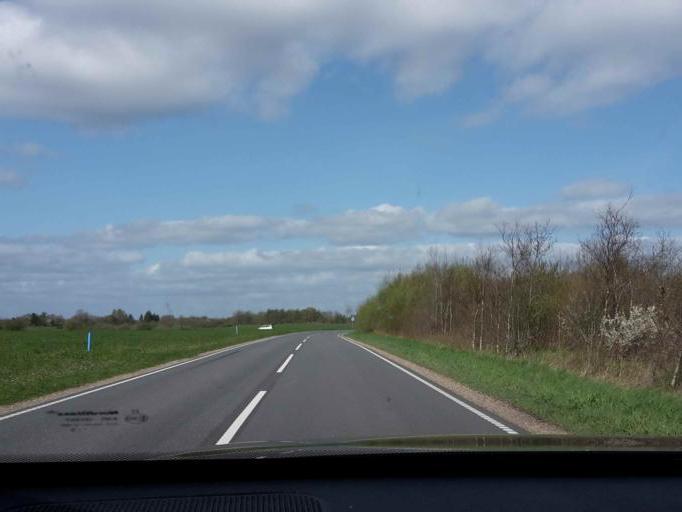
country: DK
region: South Denmark
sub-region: Billund Kommune
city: Grindsted
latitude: 55.6913
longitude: 8.8532
